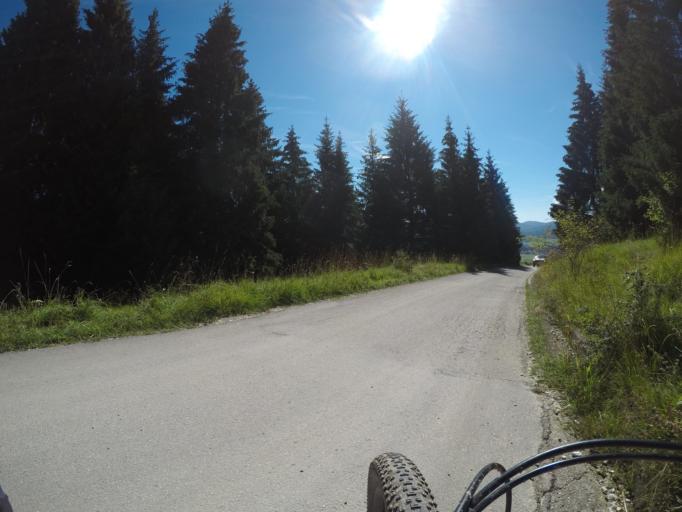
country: IT
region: Veneto
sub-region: Provincia di Vicenza
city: Canove di Roana
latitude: 45.8901
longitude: 11.4832
